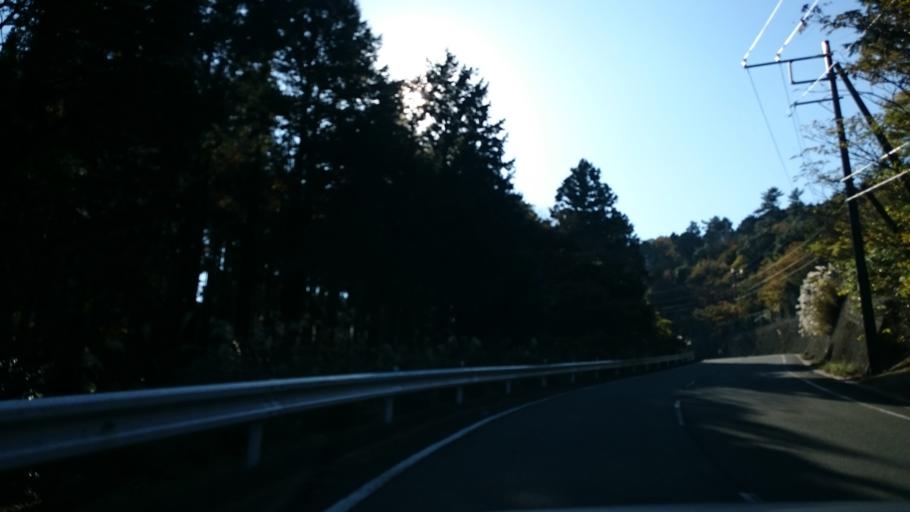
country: JP
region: Shizuoka
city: Heda
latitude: 34.9928
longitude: 138.8124
